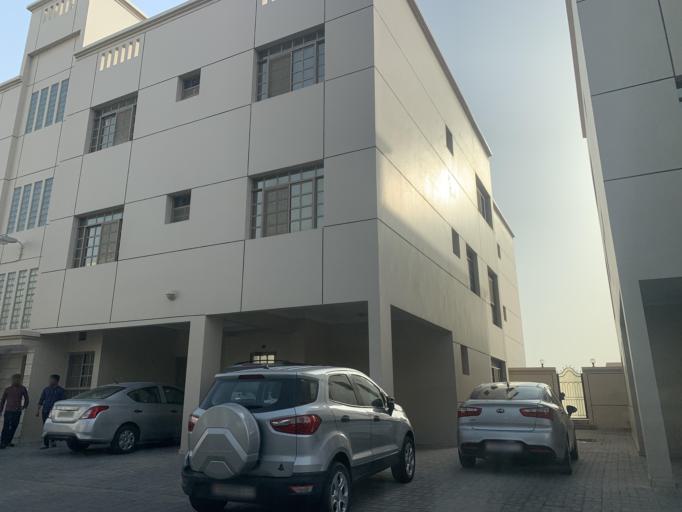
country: BH
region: Northern
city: Madinat `Isa
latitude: 26.1941
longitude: 50.5642
